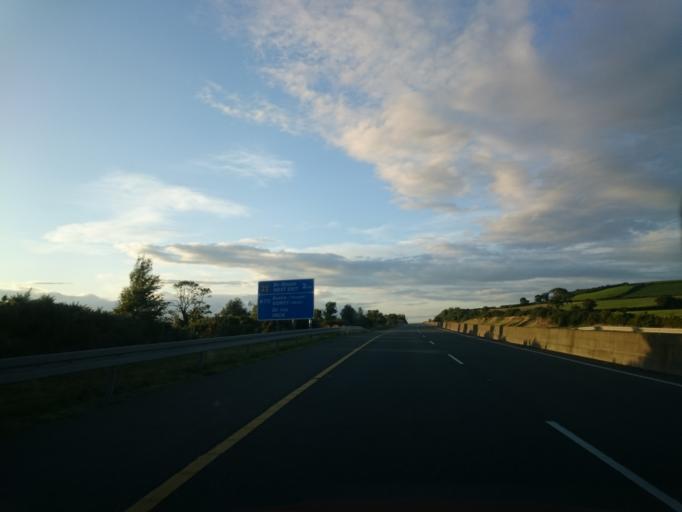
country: IE
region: Leinster
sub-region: Loch Garman
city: Gorey
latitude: 52.6910
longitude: -6.2641
